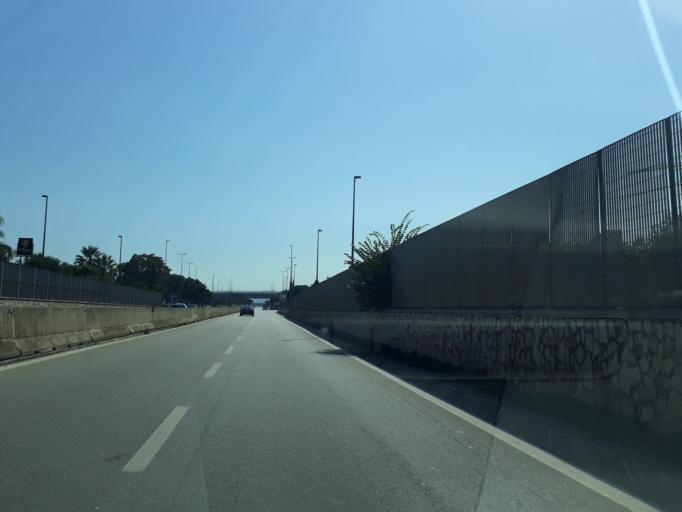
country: IT
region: Apulia
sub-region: Provincia di Brindisi
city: Fasano
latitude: 40.8837
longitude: 17.3364
